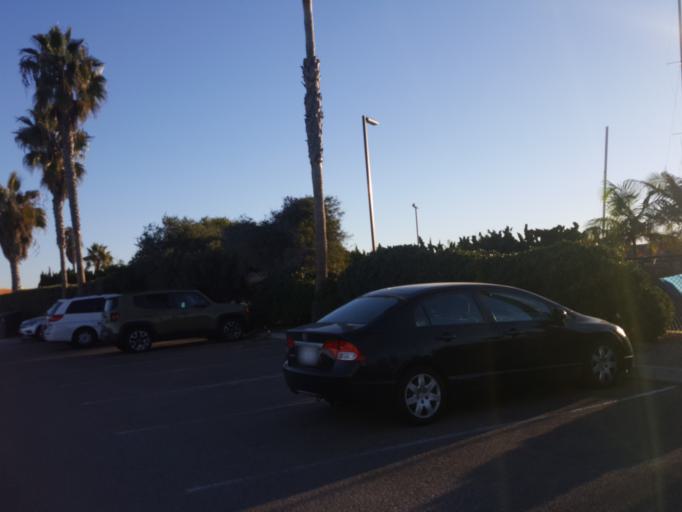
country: US
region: California
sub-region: San Diego County
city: La Jolla
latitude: 32.7788
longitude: -117.2487
